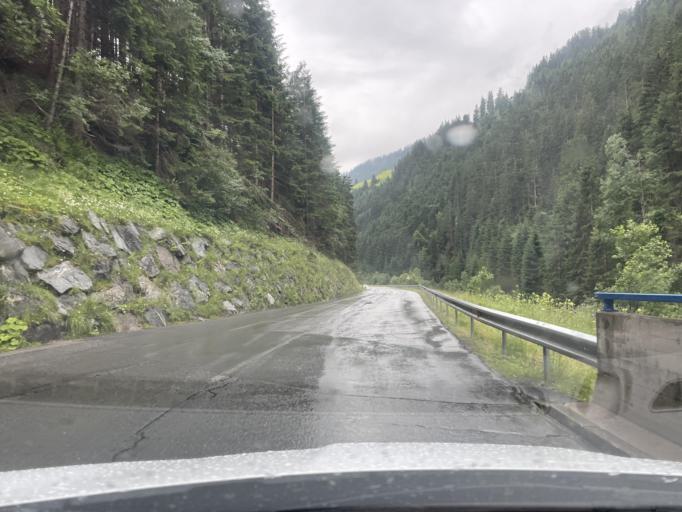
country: AT
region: Tyrol
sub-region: Politischer Bezirk Lienz
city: Ausservillgraten
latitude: 46.7805
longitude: 12.4289
